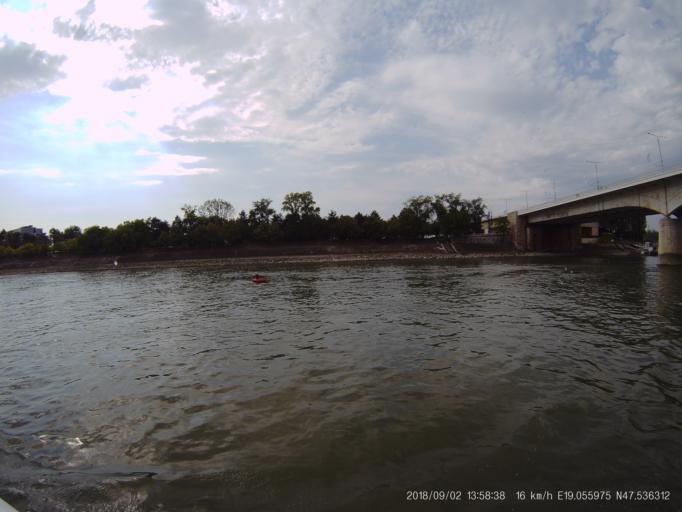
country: HU
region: Budapest
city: Budapest III. keruelet
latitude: 47.5361
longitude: 19.0560
